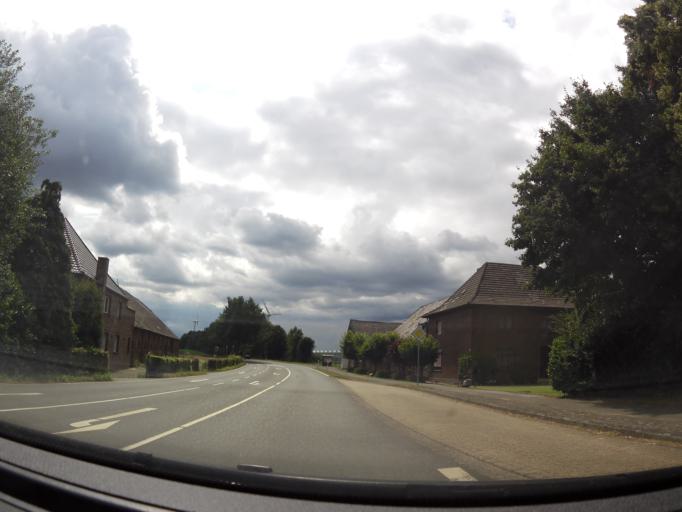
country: DE
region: North Rhine-Westphalia
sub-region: Regierungsbezirk Dusseldorf
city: Sonsbeck
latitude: 51.5683
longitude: 6.3886
